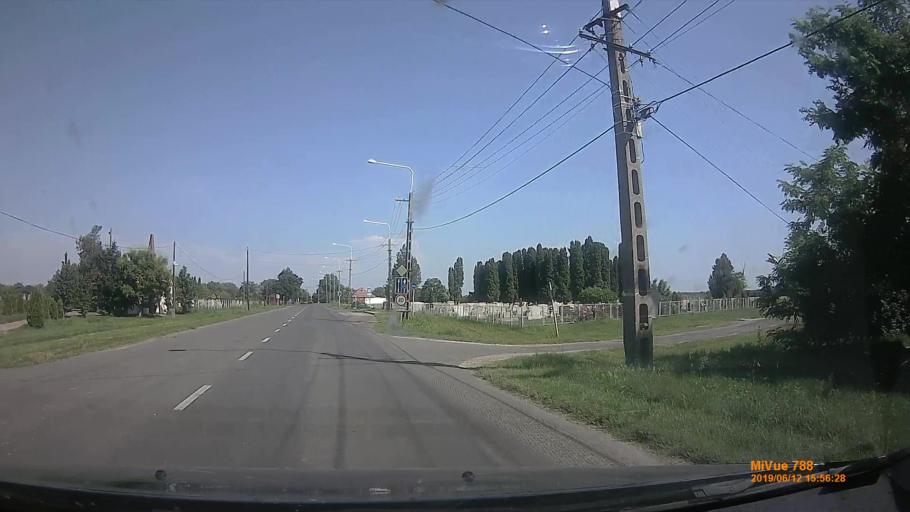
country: HU
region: Csongrad
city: Apatfalva
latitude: 46.1697
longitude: 20.6200
